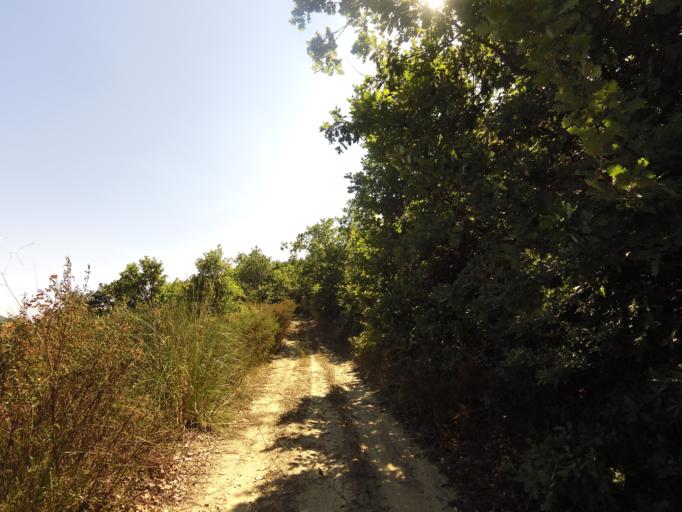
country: IT
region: Calabria
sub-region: Provincia di Reggio Calabria
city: Pazzano
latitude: 38.4599
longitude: 16.4594
